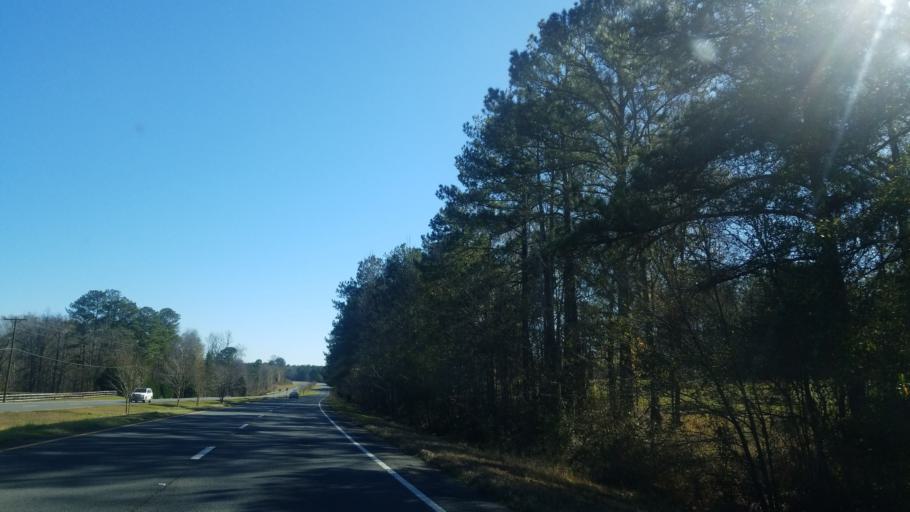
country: US
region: Georgia
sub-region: Talbot County
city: Talbotton
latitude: 32.5500
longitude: -84.7343
